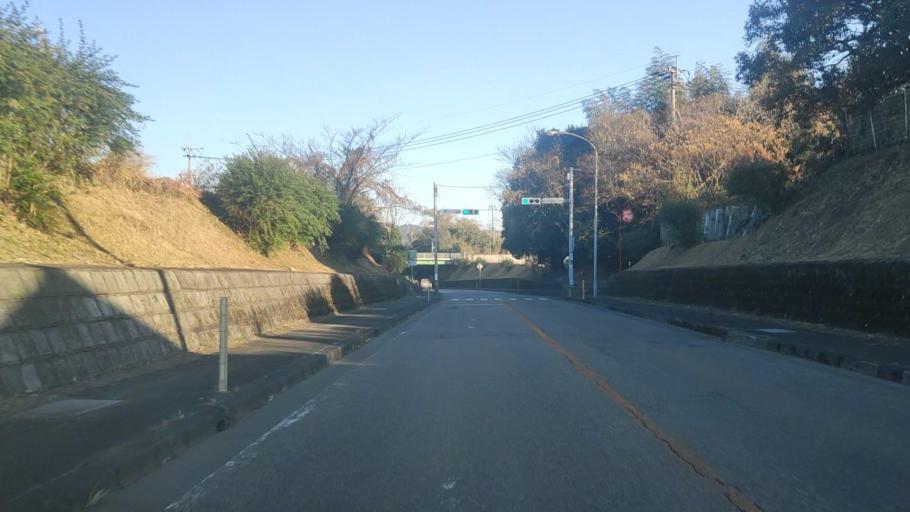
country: JP
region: Miyazaki
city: Takanabe
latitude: 32.2339
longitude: 131.5486
